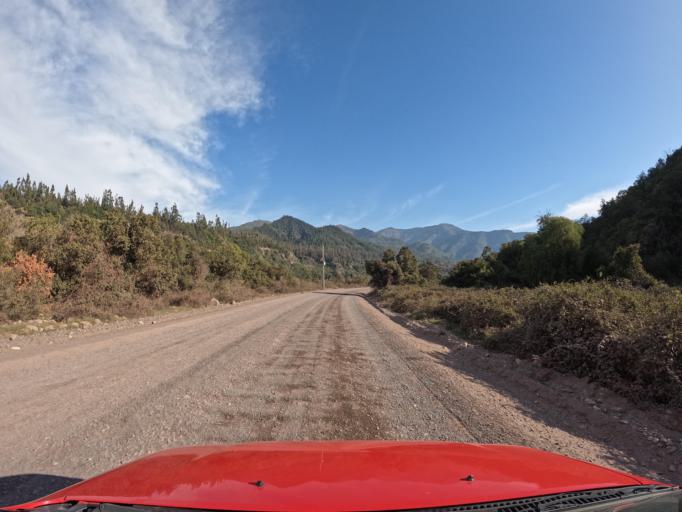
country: CL
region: Maule
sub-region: Provincia de Curico
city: Teno
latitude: -34.9999
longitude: -70.8265
